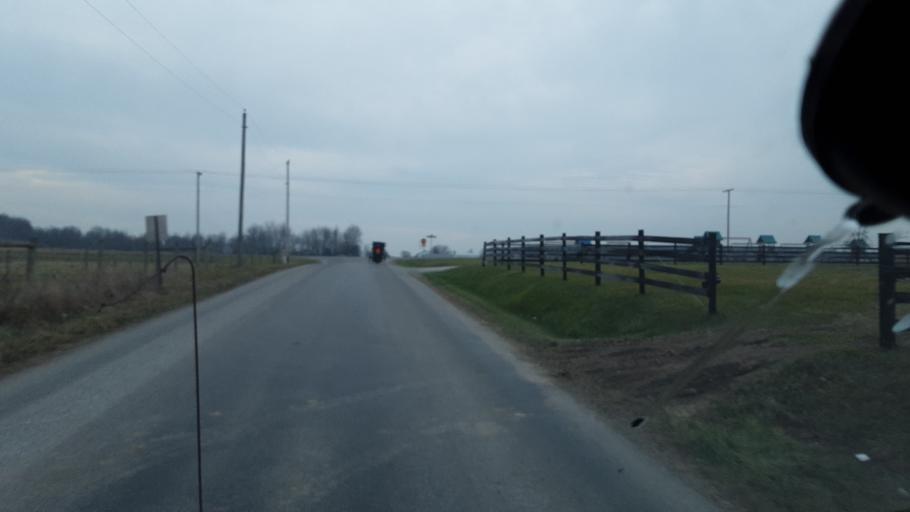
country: US
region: Indiana
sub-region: Elkhart County
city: Middlebury
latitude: 41.6775
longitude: -85.6196
